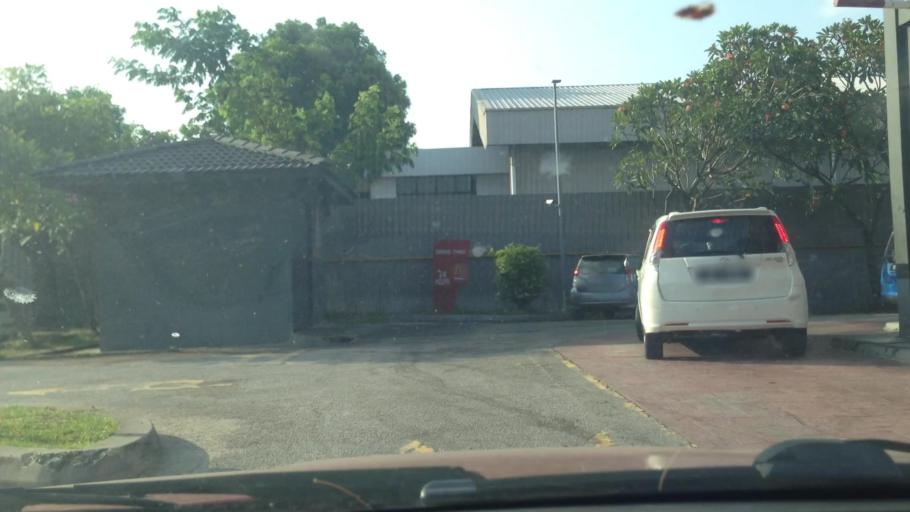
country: MY
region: Selangor
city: Subang Jaya
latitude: 3.0403
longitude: 101.5474
